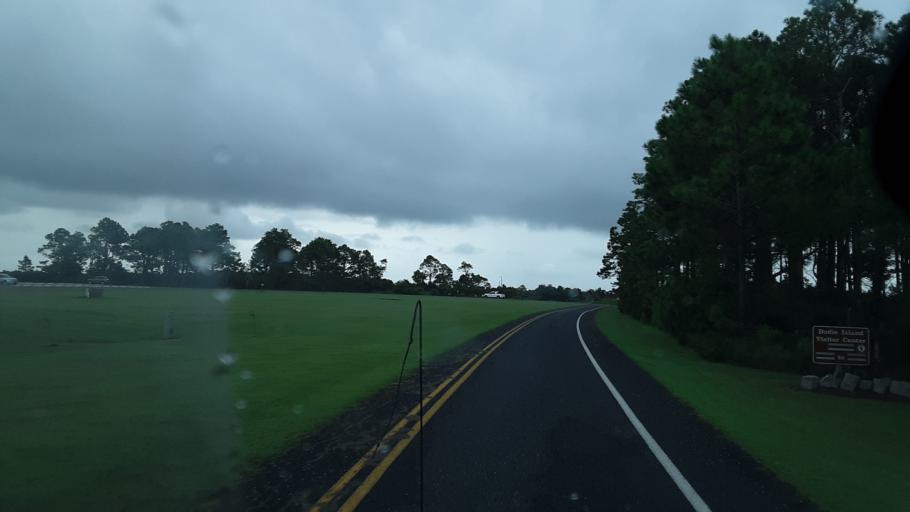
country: US
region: North Carolina
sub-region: Dare County
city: Wanchese
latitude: 35.8187
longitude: -75.5653
